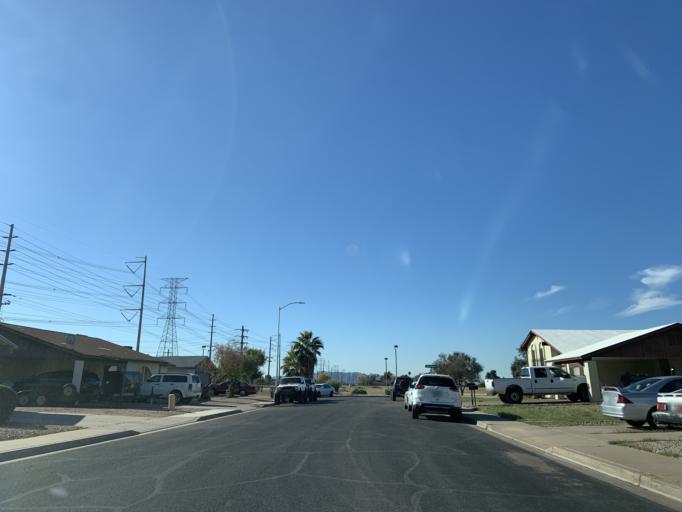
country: US
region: Arizona
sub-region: Maricopa County
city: San Carlos
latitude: 33.3574
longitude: -111.8718
